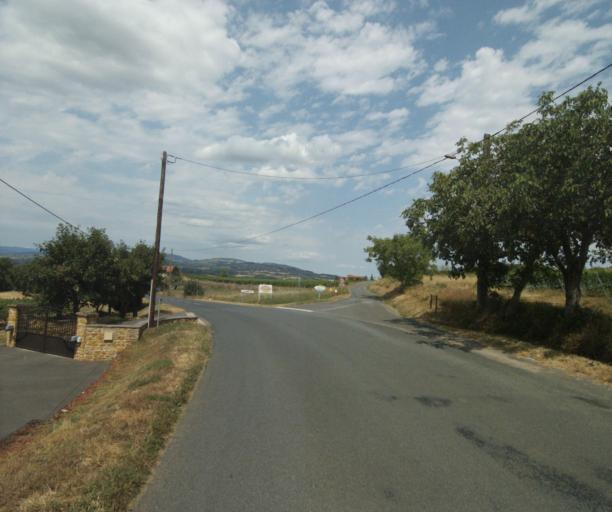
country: FR
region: Rhone-Alpes
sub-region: Departement du Rhone
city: Chatillon
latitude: 45.8760
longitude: 4.6043
